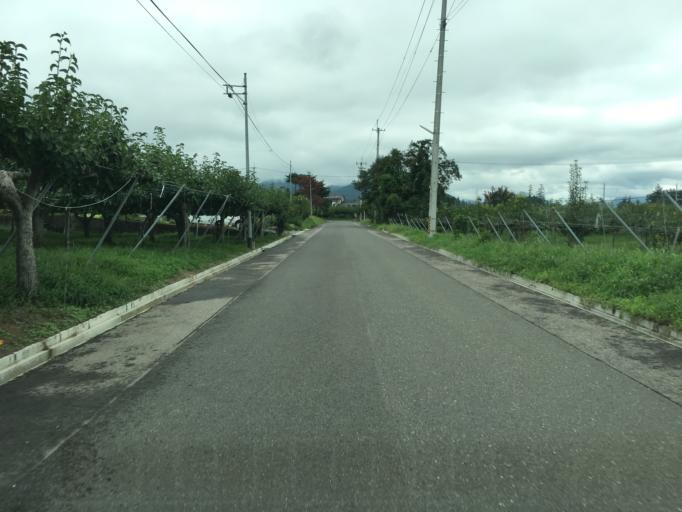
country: JP
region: Fukushima
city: Fukushima-shi
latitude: 37.7741
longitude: 140.4061
